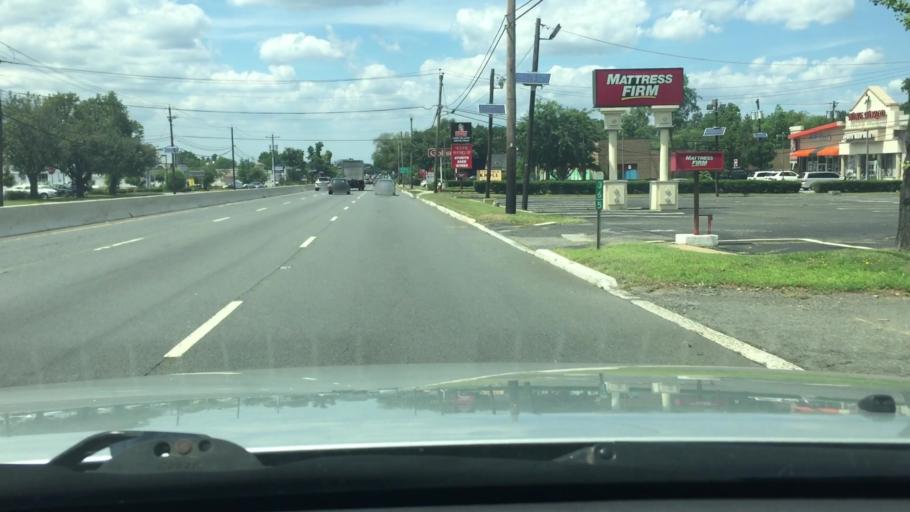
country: US
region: New Jersey
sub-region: Middlesex County
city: South River
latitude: 40.4306
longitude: -74.3852
